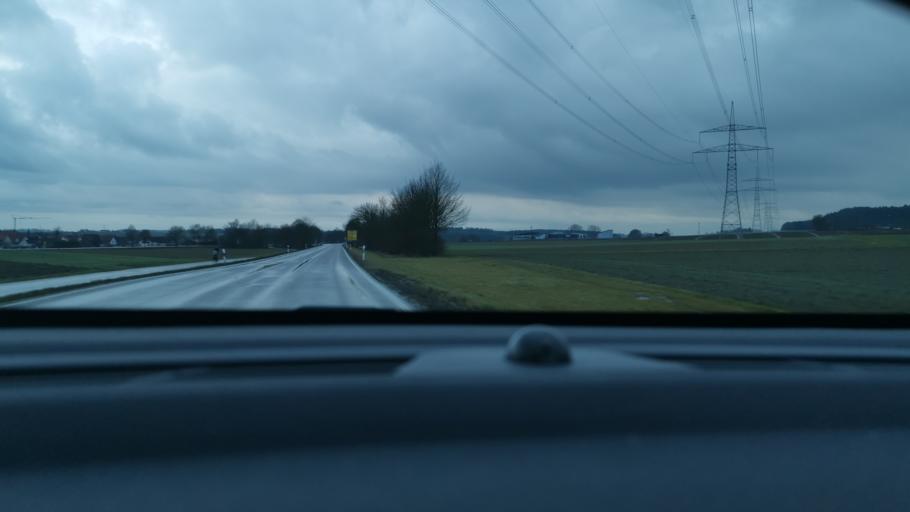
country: DE
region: Bavaria
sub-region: Swabia
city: Petersdorf
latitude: 48.5143
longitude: 11.0228
